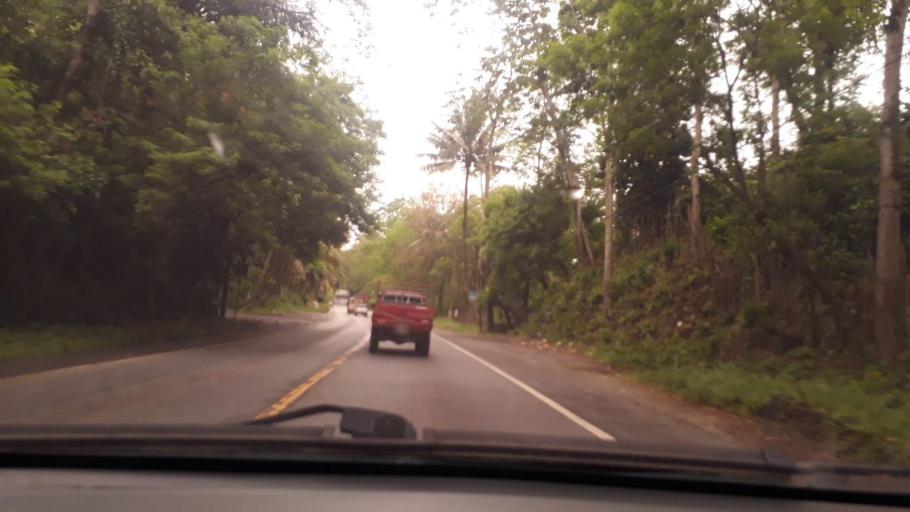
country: GT
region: Izabal
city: Morales
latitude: 15.5374
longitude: -88.7467
